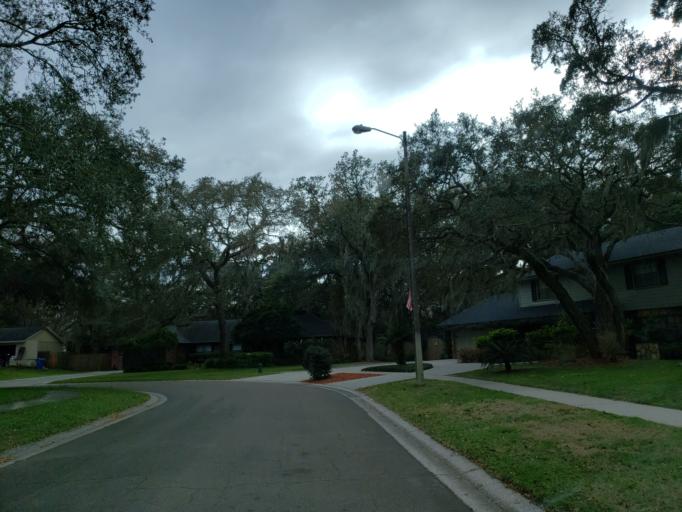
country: US
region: Florida
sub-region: Hillsborough County
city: Riverview
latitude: 27.8816
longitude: -82.2851
